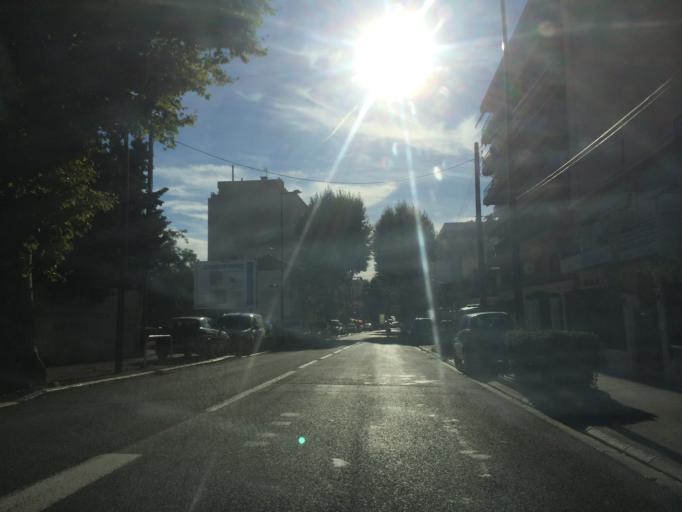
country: FR
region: Provence-Alpes-Cote d'Azur
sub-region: Departement des Alpes-Maritimes
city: Antibes
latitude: 43.5715
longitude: 7.1118
